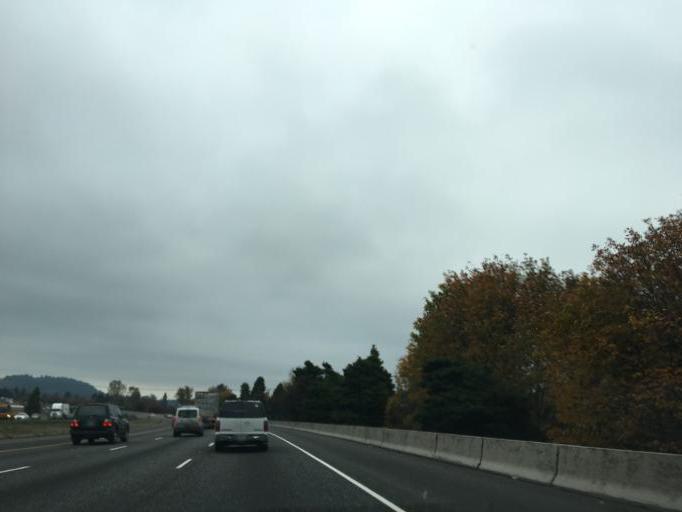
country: US
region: Oregon
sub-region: Multnomah County
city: Lents
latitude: 45.4656
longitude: -122.5672
